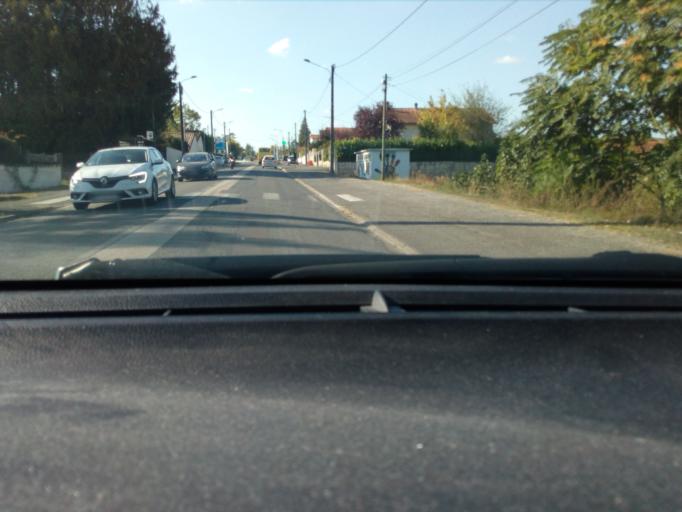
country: FR
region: Poitou-Charentes
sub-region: Departement de la Charente
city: Saint-Yrieix-sur-Charente
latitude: 45.6719
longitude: 0.1273
